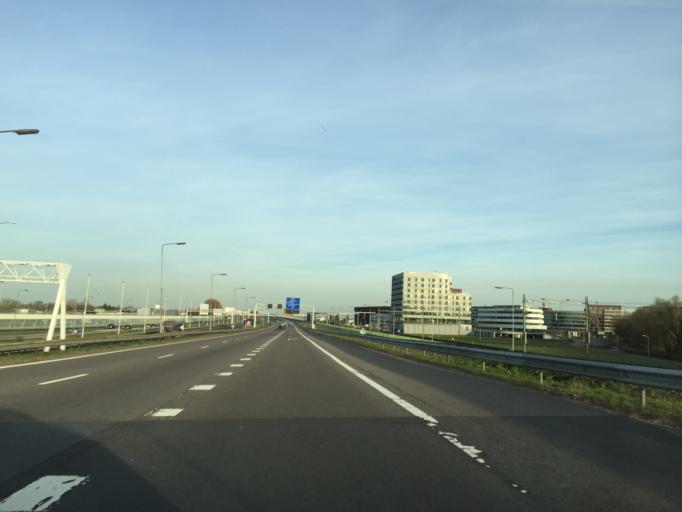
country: NL
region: South Holland
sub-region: Gemeente Den Haag
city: Ypenburg
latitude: 52.0586
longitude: 4.3837
